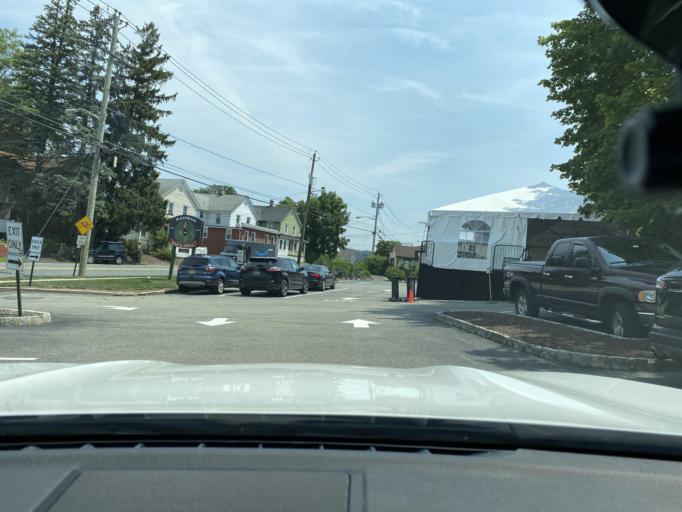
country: US
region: New York
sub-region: Rockland County
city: Suffern
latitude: 41.1023
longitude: -74.1534
